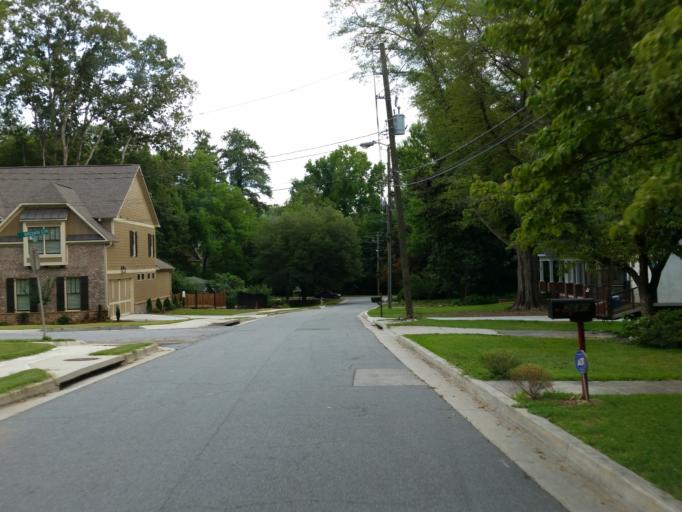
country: US
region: Georgia
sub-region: Cobb County
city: Smyrna
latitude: 33.8877
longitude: -84.5202
